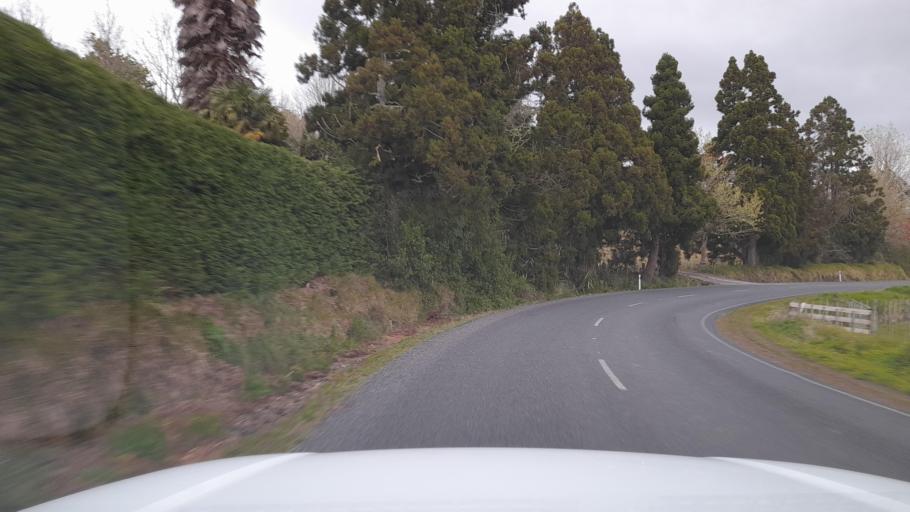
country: NZ
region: Northland
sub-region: Whangarei
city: Maungatapere
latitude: -35.6388
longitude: 174.2162
